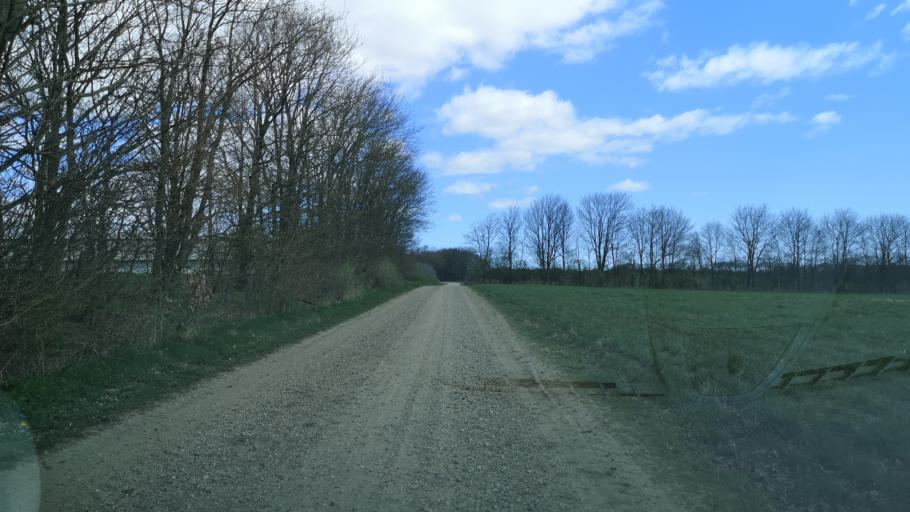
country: DK
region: Central Jutland
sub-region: Ringkobing-Skjern Kommune
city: Skjern
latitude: 55.9730
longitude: 8.5033
